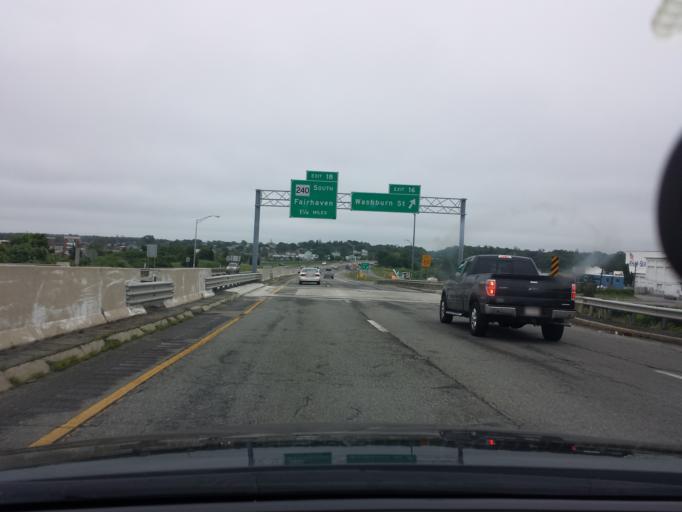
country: US
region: Massachusetts
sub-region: Bristol County
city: New Bedford
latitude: 41.6546
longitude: -70.9240
